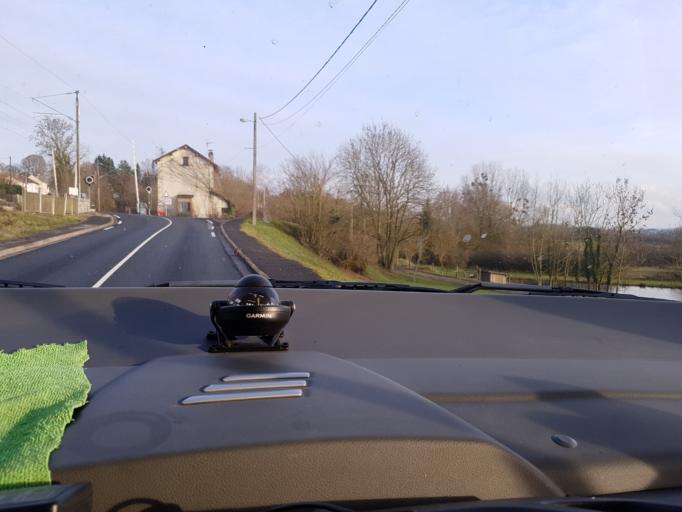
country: FR
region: Champagne-Ardenne
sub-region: Departement des Ardennes
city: Warcq
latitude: 49.7776
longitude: 4.6902
